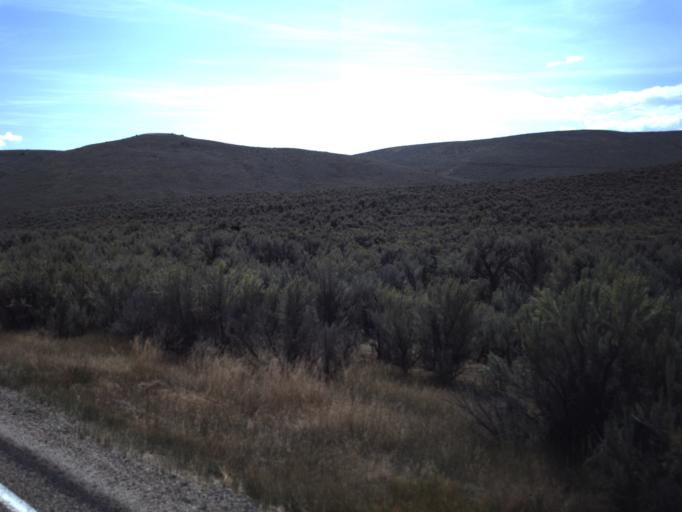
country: US
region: Utah
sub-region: Rich County
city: Randolph
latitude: 41.7727
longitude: -111.1764
